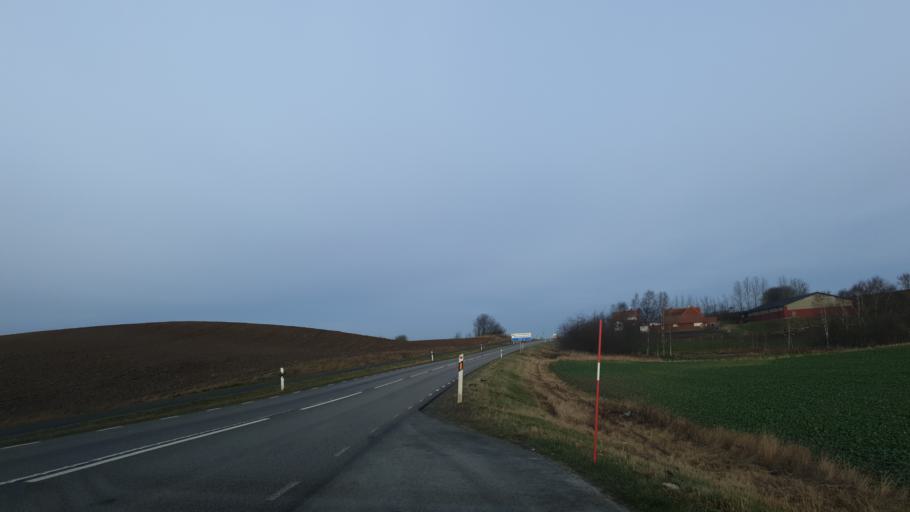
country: SE
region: Skane
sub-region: Ystads Kommun
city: Ystad
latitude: 55.4580
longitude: 13.7983
